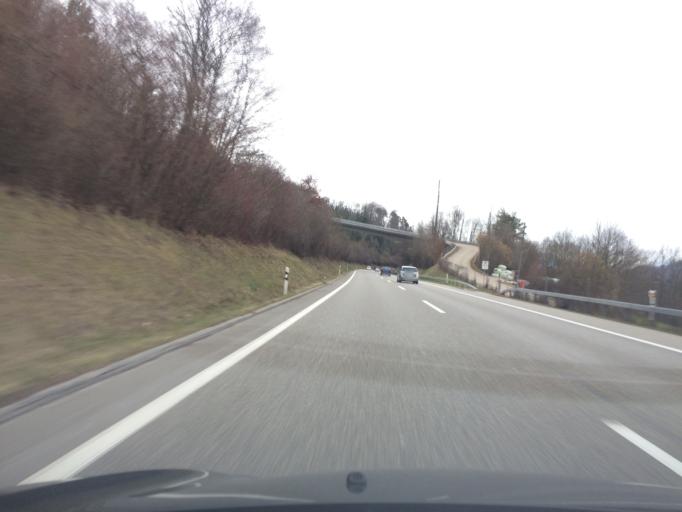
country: CH
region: Bern
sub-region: Bern-Mittelland District
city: Belp
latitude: 46.9116
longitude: 7.5159
